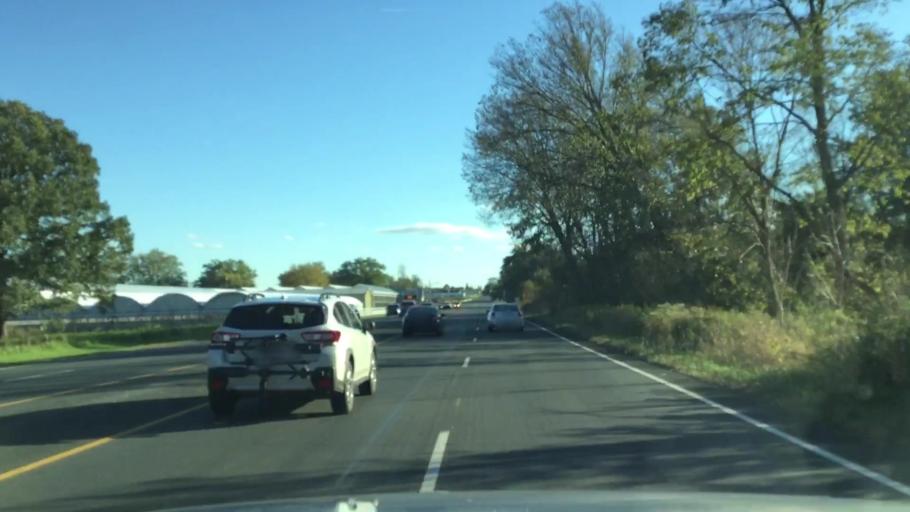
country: US
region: Michigan
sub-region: Kalamazoo County
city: Eastwood
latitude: 42.2805
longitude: -85.5308
